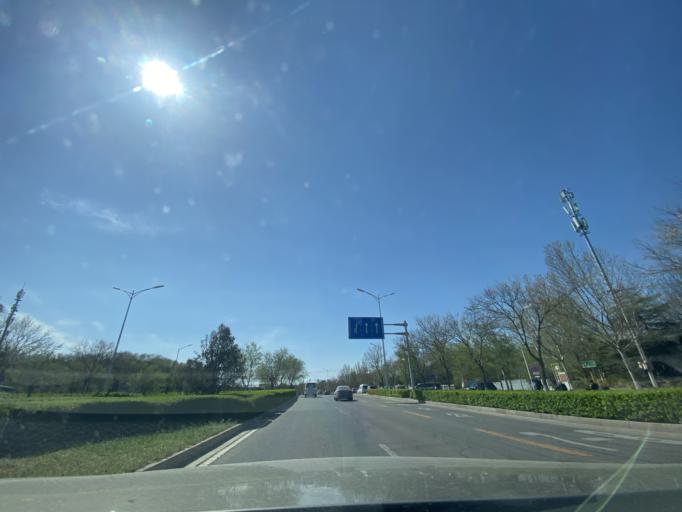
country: CN
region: Beijing
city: Sijiqing
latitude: 39.9402
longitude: 116.2403
